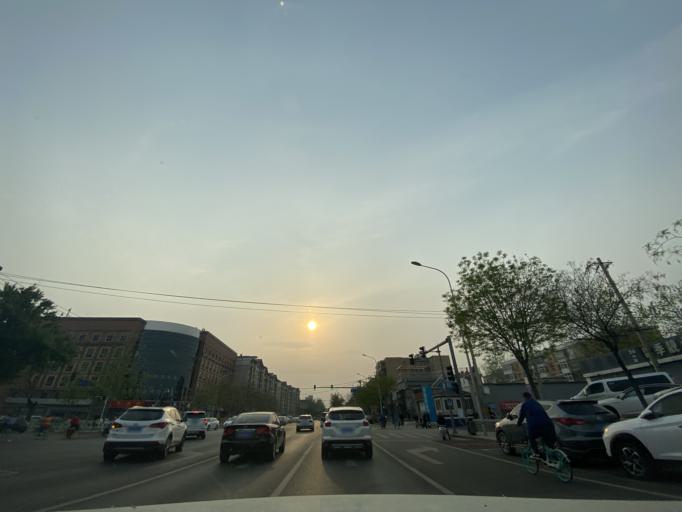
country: CN
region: Beijing
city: Sijiqing
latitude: 39.9279
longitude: 116.2591
